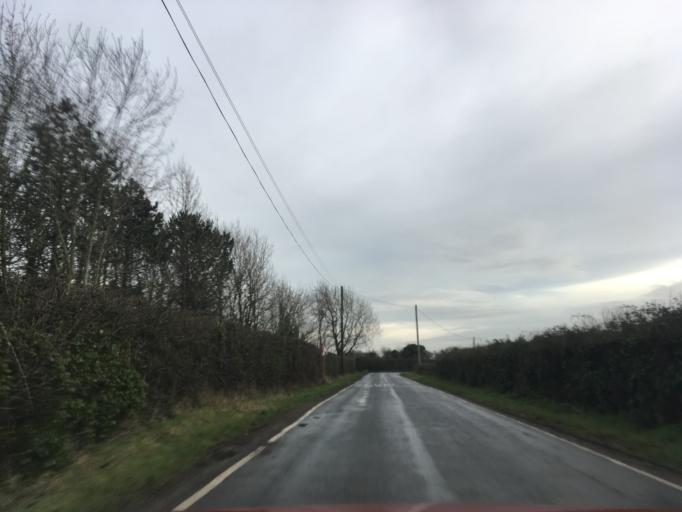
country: GB
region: Wales
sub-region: Newport
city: Goldcliff
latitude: 51.5484
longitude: -2.9002
